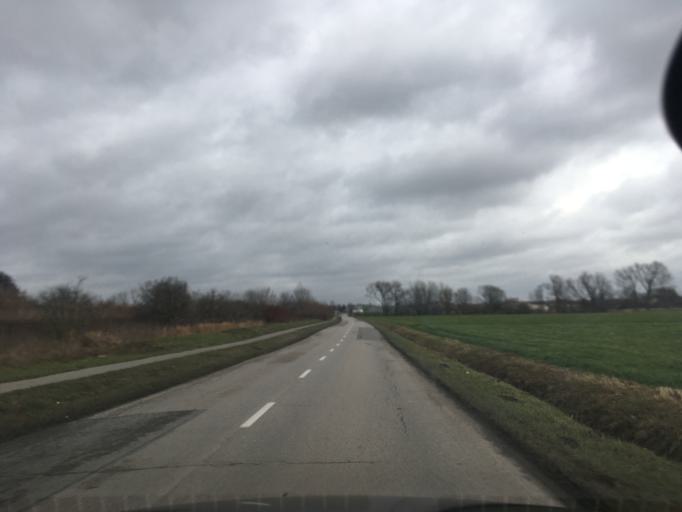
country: PL
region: Masovian Voivodeship
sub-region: Powiat pruszkowski
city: Rybie
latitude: 52.1307
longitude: 20.9681
